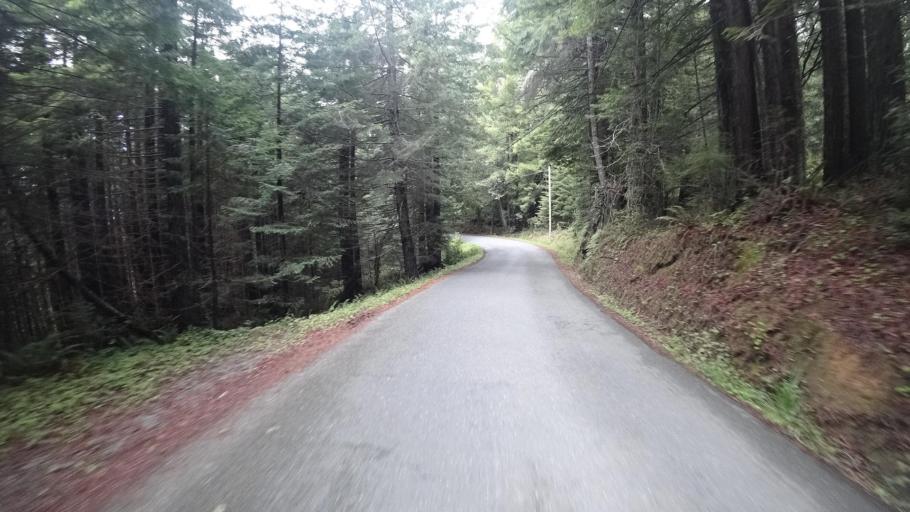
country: US
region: California
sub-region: Humboldt County
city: Blue Lake
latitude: 40.8510
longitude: -123.9282
